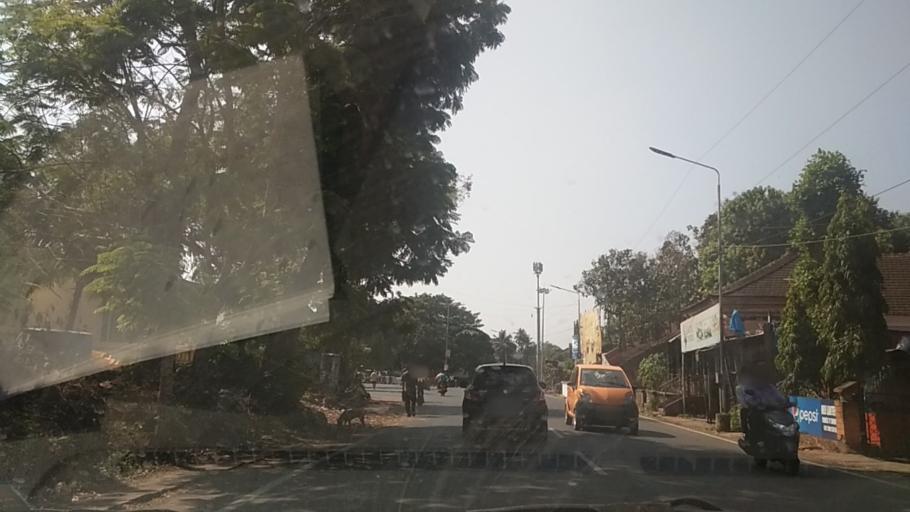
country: IN
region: Goa
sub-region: South Goa
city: Madgaon
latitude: 15.2817
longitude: 73.9608
